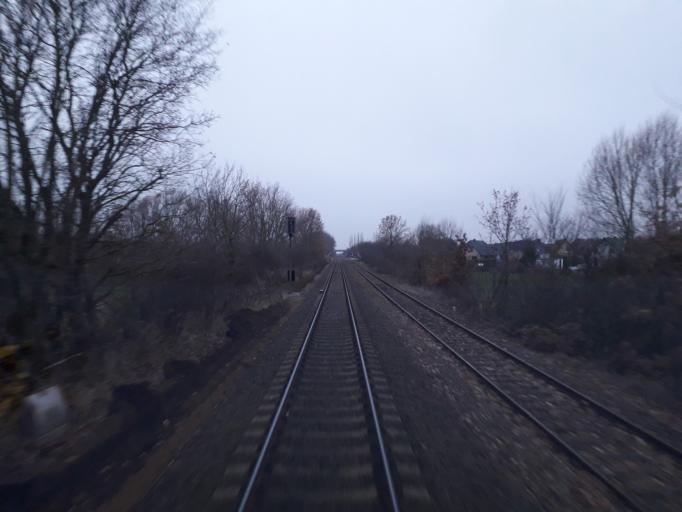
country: DE
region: Brandenburg
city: Pritzwalk
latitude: 53.1446
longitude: 12.1680
